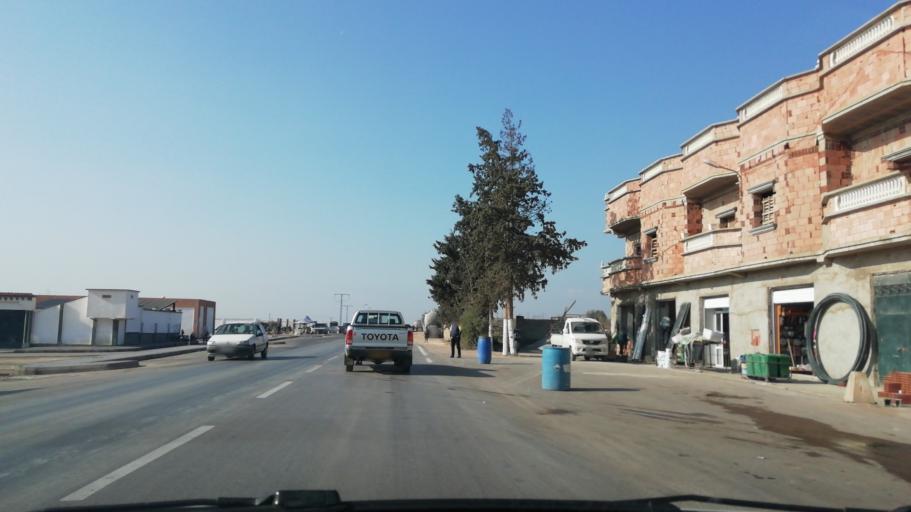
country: DZ
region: Mostaganem
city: Mostaganem
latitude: 35.7373
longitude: -0.0311
